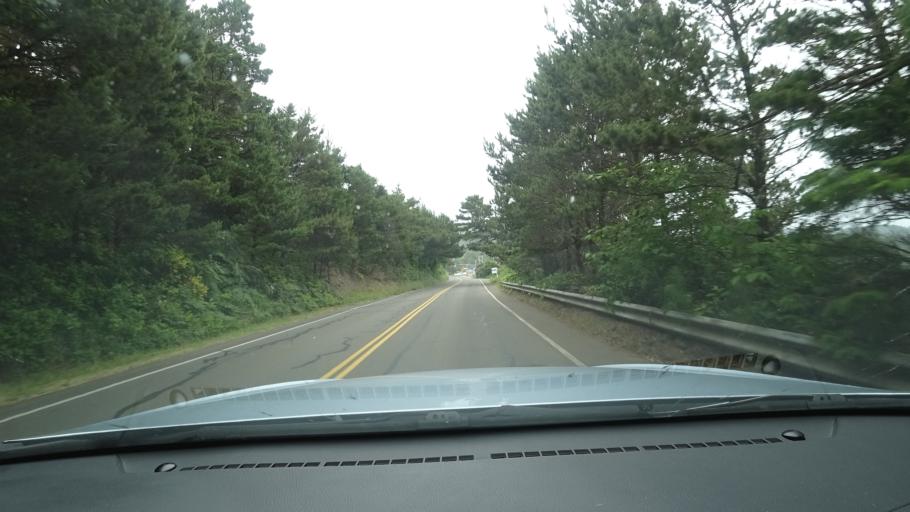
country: US
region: Oregon
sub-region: Lincoln County
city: Newport
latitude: 44.6755
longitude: -124.0636
